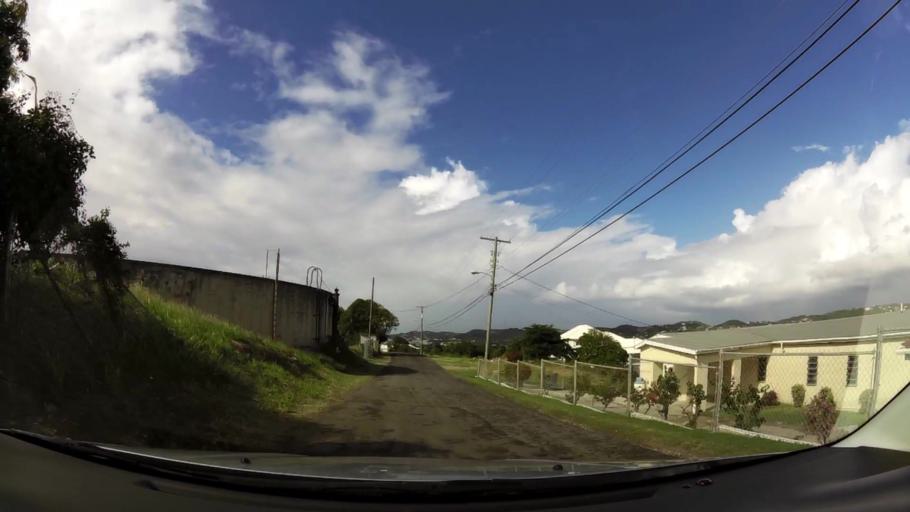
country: AG
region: Saint John
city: Saint John's
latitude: 17.1127
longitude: -61.8256
